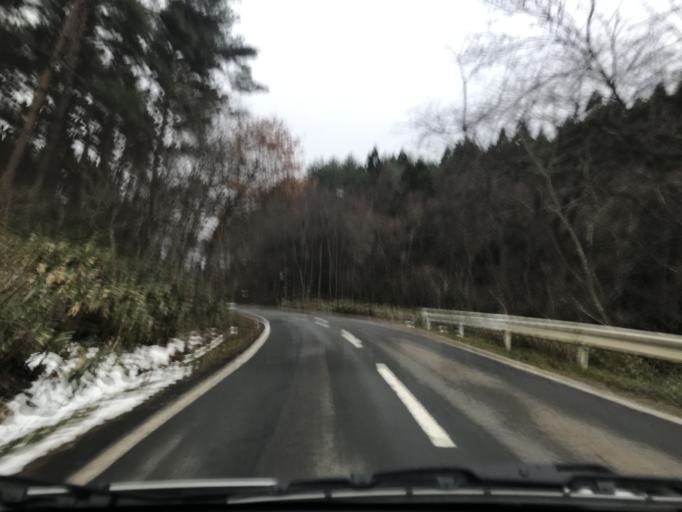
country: JP
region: Iwate
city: Mizusawa
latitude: 39.1509
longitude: 141.3620
